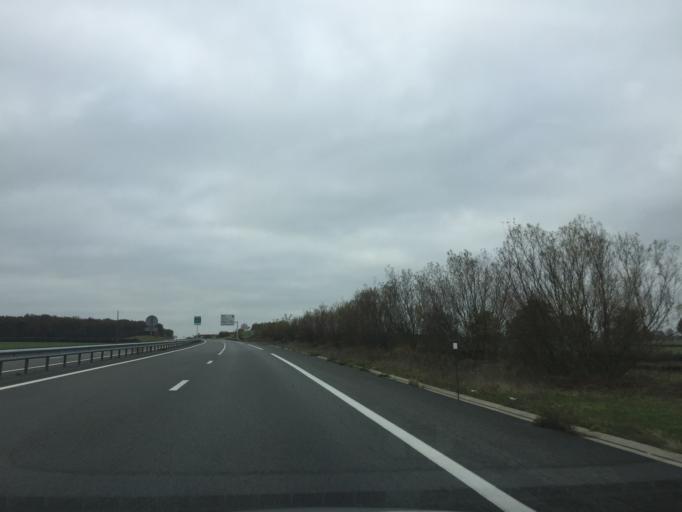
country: FR
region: Limousin
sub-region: Departement de la Creuse
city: Chambon-sur-Voueize
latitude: 46.2628
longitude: 2.3665
